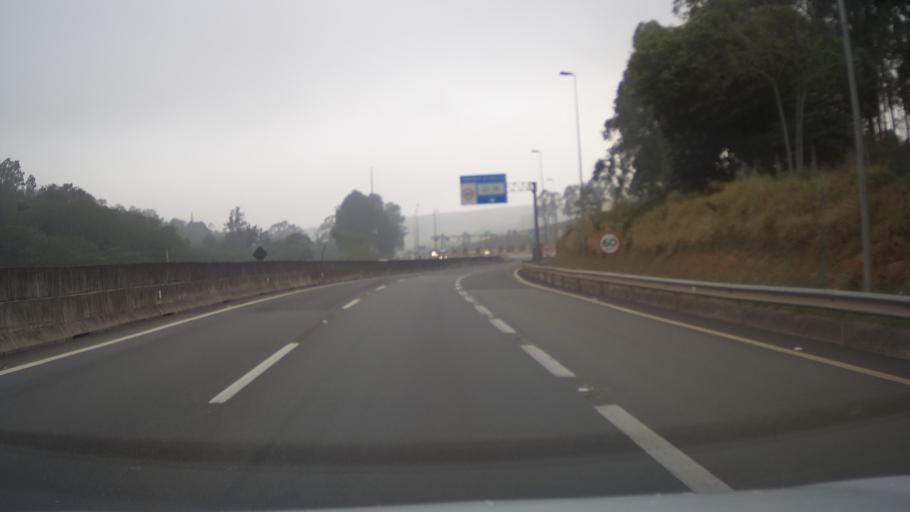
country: BR
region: Sao Paulo
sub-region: Itatiba
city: Itatiba
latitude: -23.0795
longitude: -46.8434
